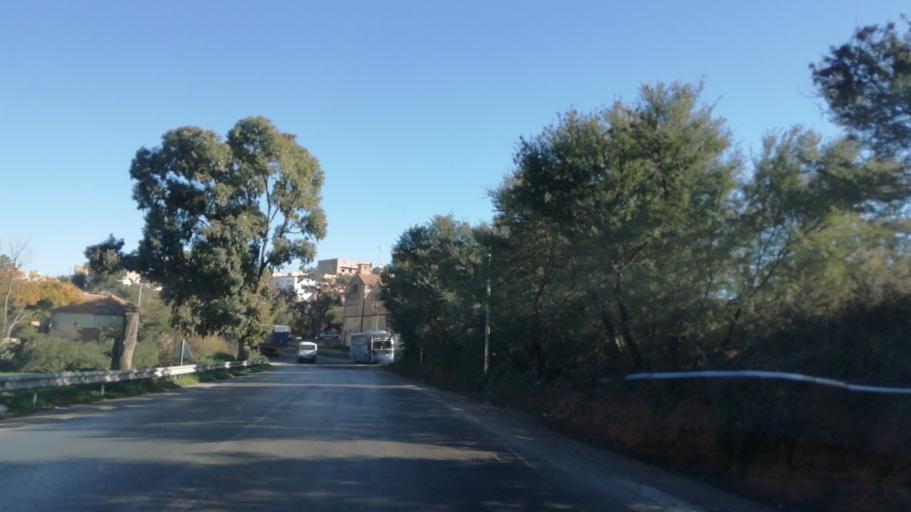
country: DZ
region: Relizane
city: Smala
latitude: 35.6560
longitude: 0.8189
